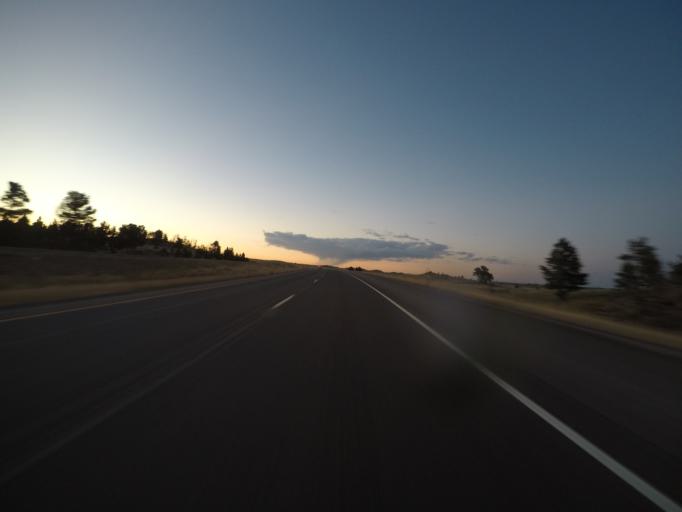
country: US
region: Wyoming
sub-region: Albany County
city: Laramie
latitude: 41.0122
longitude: -105.4195
